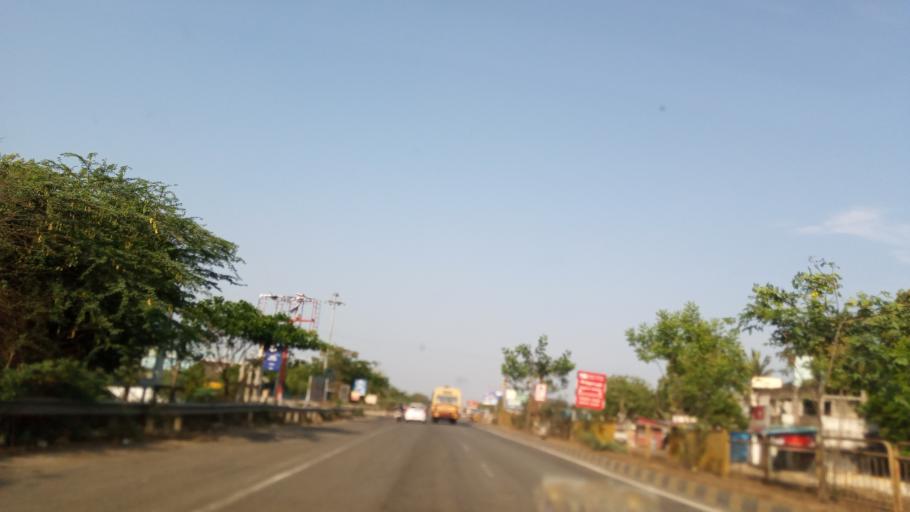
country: IN
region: Tamil Nadu
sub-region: Kancheepuram
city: Poonamalle
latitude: 13.0398
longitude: 80.0552
